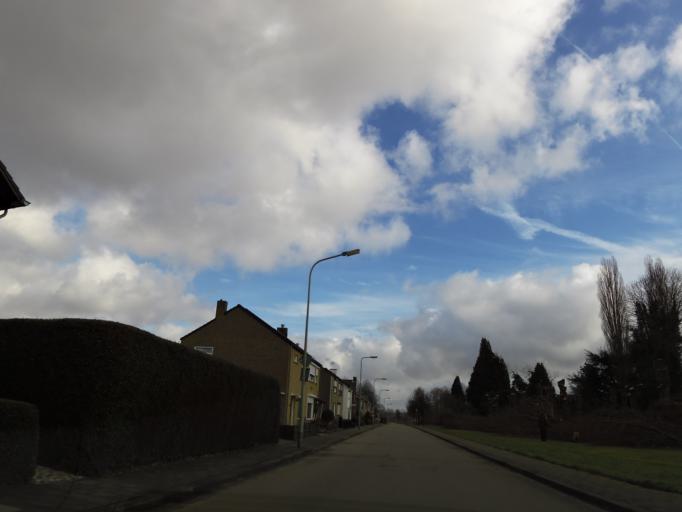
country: NL
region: Limburg
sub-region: Gemeente Maastricht
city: Maastricht
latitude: 50.8780
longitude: 5.6851
